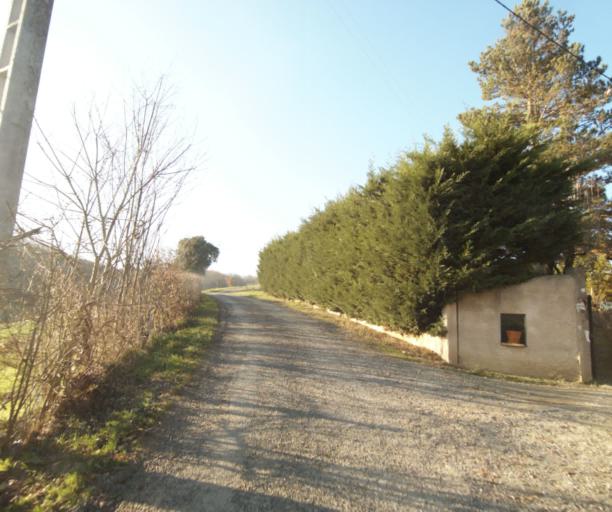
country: FR
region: Midi-Pyrenees
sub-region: Departement du Tarn-et-Garonne
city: Moissac
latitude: 44.1383
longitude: 1.1288
